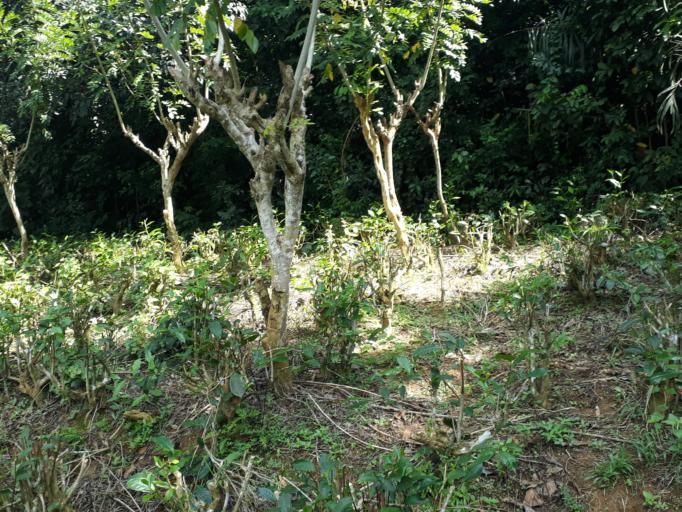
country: LK
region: Southern
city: Talpe
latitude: 6.0354
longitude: 80.2855
